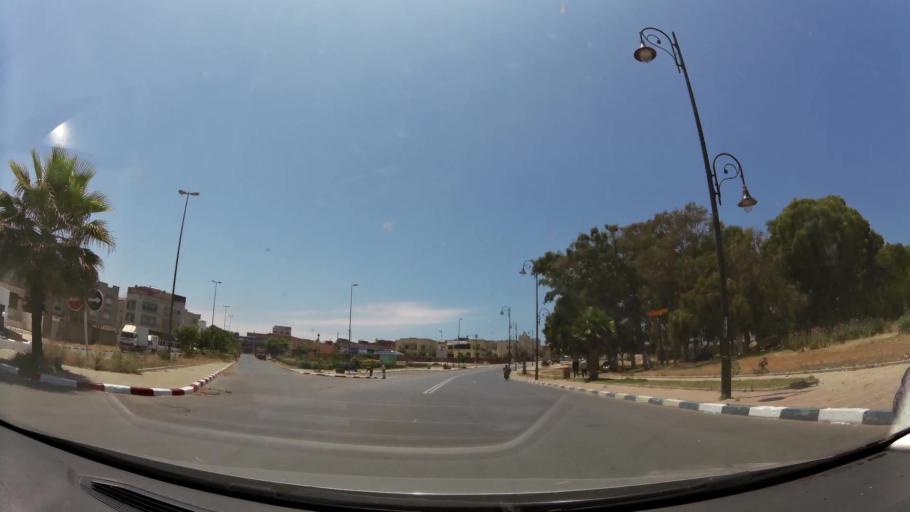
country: MA
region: Gharb-Chrarda-Beni Hssen
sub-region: Kenitra Province
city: Kenitra
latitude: 34.2675
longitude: -6.6438
